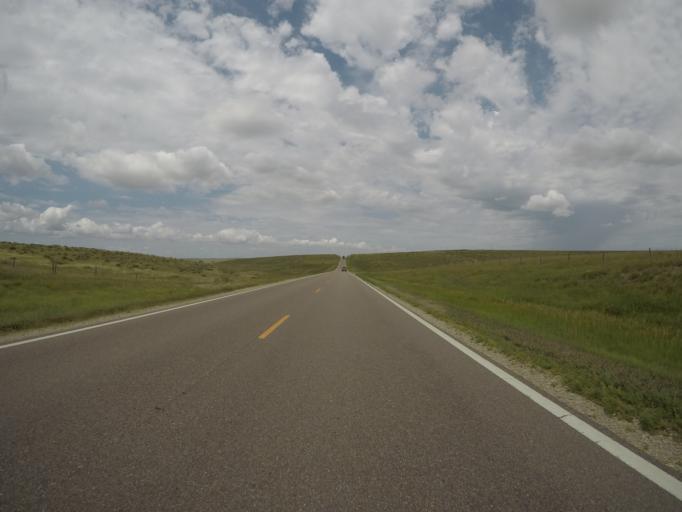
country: US
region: Kansas
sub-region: Rawlins County
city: Atwood
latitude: 39.7384
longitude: -101.0536
